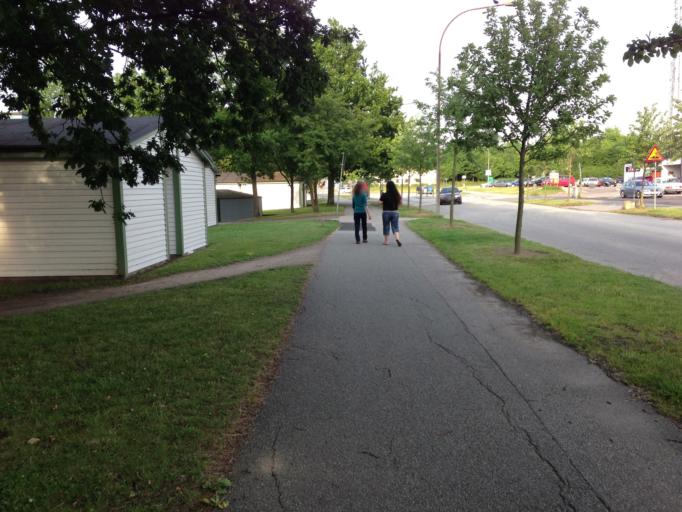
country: SE
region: Skane
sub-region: Lunds Kommun
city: Lund
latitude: 55.7207
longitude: 13.2198
